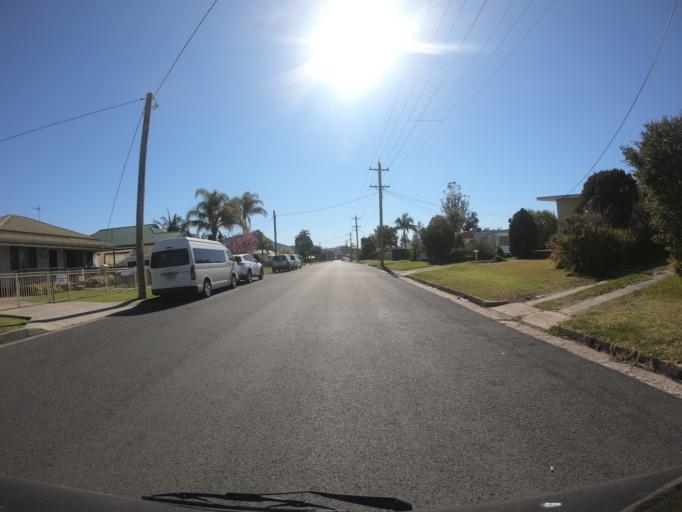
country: AU
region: New South Wales
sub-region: Wollongong
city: Dapto
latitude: -34.4924
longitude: 150.7909
